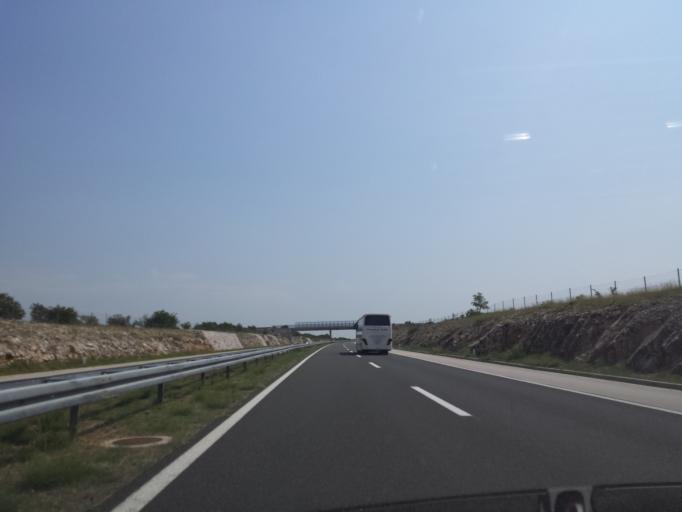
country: HR
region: Zadarska
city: Polaca
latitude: 44.0892
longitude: 15.4947
